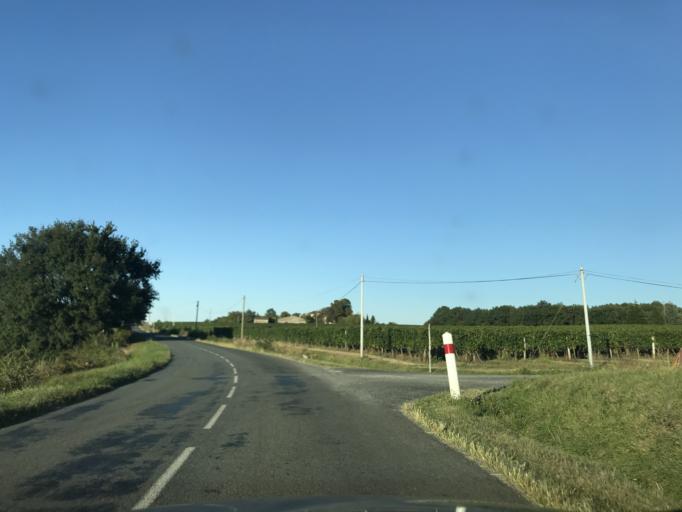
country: FR
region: Aquitaine
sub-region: Departement de la Gironde
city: Mouliets-et-Villemartin
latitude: 44.7828
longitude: -0.0505
